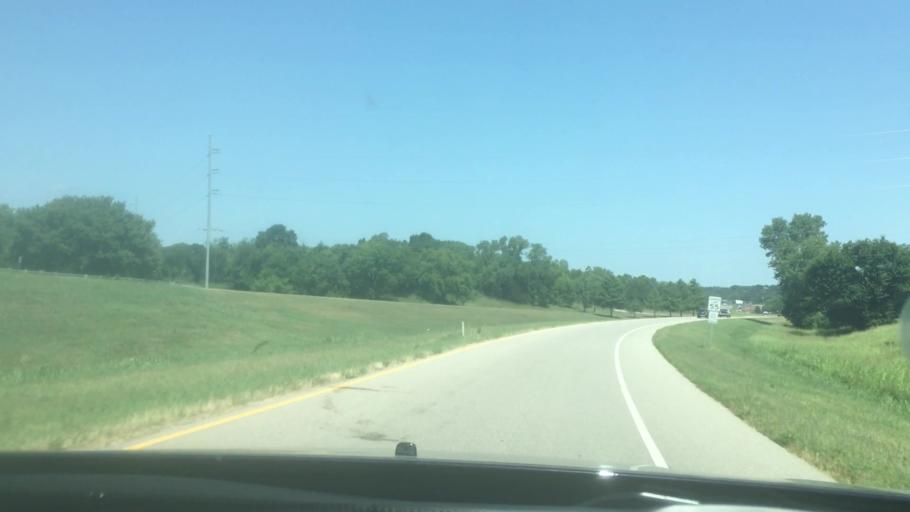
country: US
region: Oklahoma
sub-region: Pontotoc County
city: Ada
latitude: 34.7500
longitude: -96.6559
